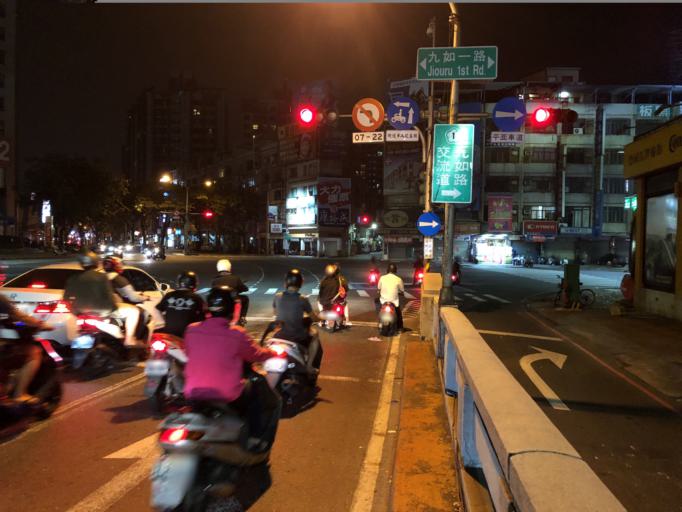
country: TW
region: Kaohsiung
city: Kaohsiung
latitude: 22.6387
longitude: 120.3279
